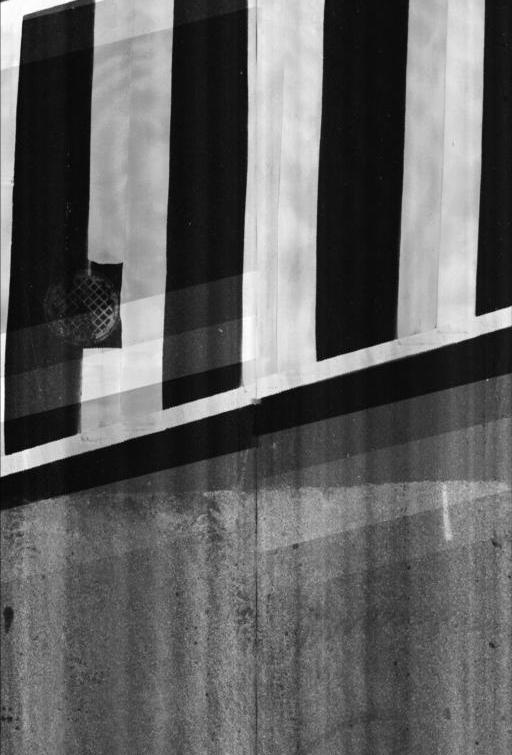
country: US
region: Maryland
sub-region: Prince George's County
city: Coral Hills
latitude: 38.8765
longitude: -76.9360
